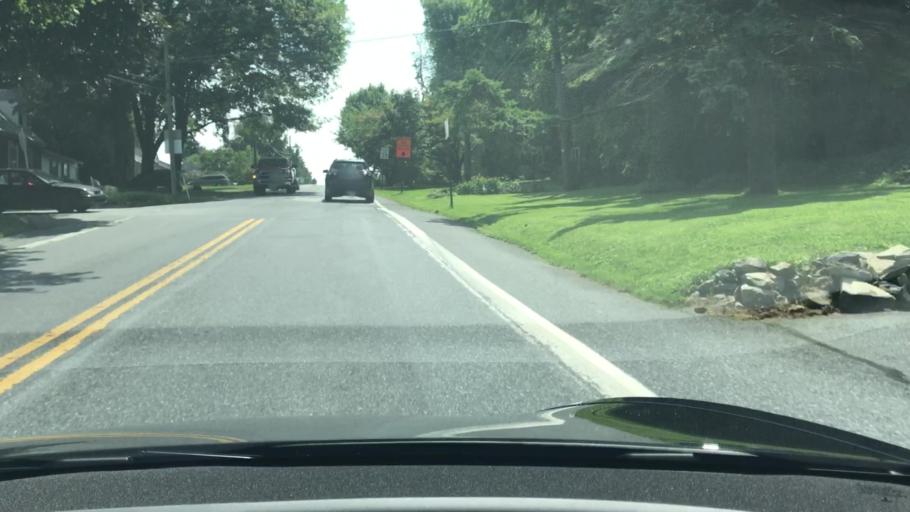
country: US
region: Pennsylvania
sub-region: Lancaster County
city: Landisville
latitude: 40.0810
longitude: -76.4084
